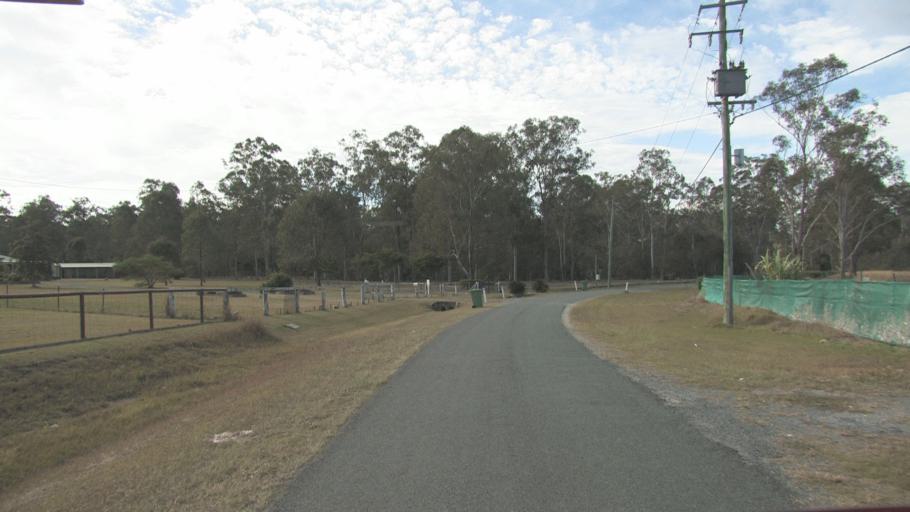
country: AU
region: Queensland
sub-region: Logan
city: North Maclean
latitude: -27.7542
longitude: 152.9839
